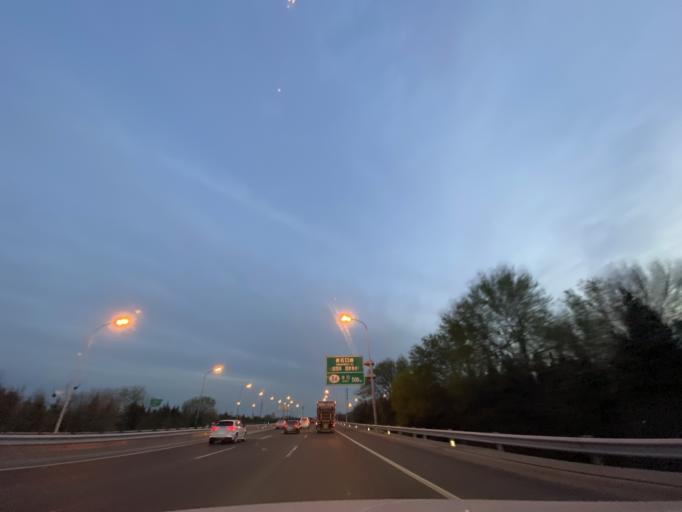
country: CN
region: Beijing
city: Xiangshan
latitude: 39.9592
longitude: 116.2113
